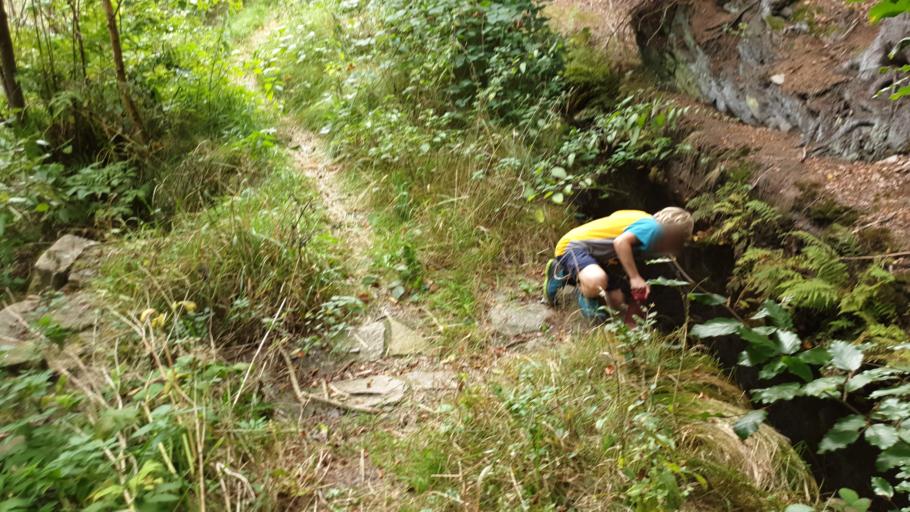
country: DE
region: Saxony
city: Pobershau
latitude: 50.6359
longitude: 13.2449
